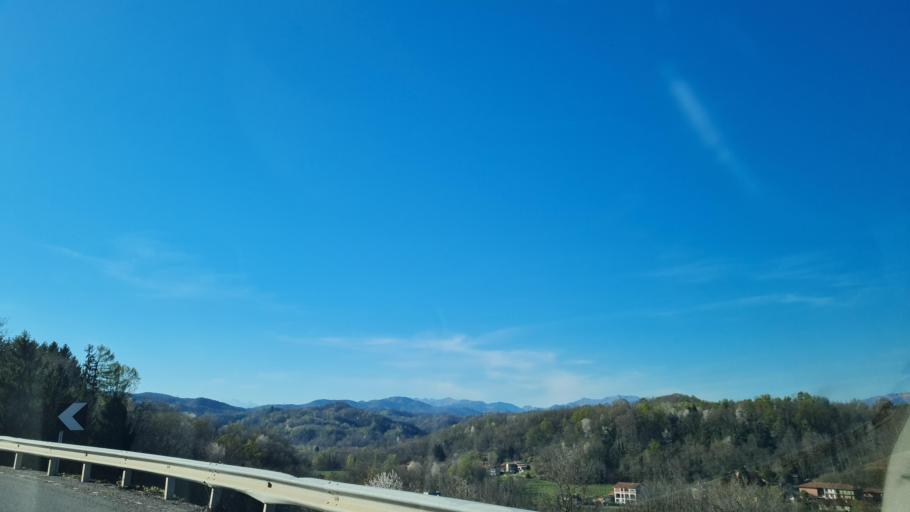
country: IT
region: Piedmont
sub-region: Provincia di Novara
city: Maggiora
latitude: 45.6905
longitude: 8.4283
